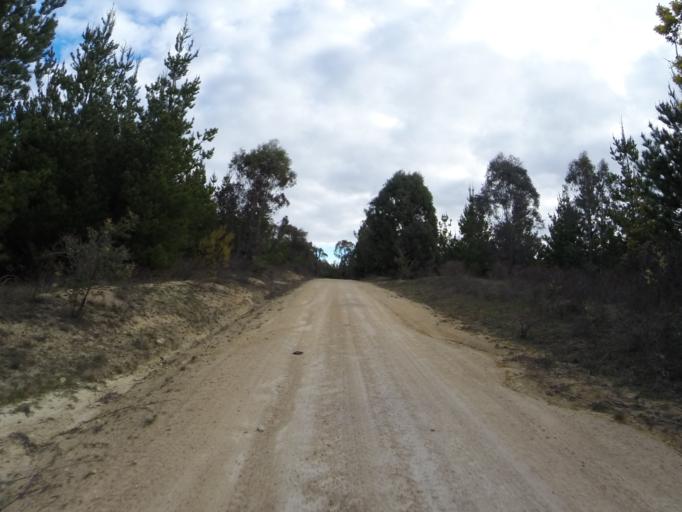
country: AU
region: Australian Capital Territory
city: Macquarie
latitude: -35.3447
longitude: 148.9316
